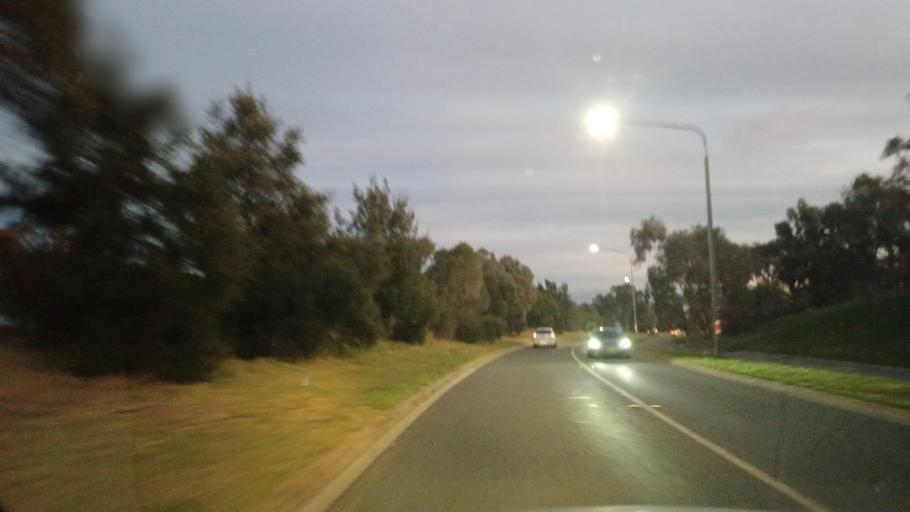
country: AU
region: Australian Capital Territory
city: Belconnen
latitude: -35.1903
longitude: 149.0713
